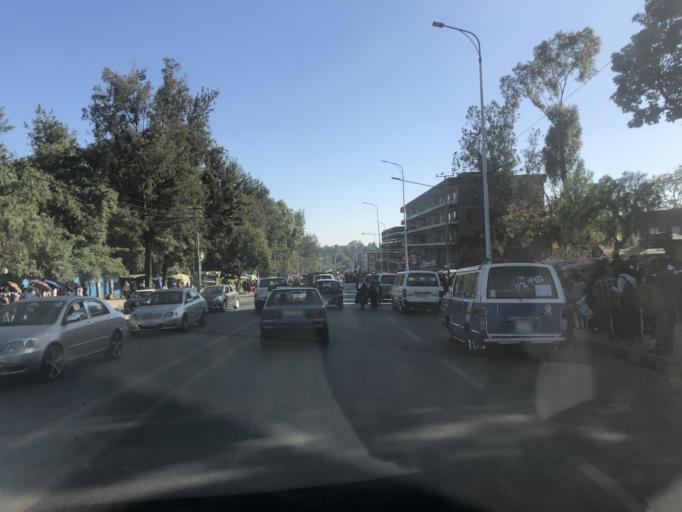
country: ET
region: Adis Abeba
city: Addis Ababa
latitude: 9.0362
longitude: 38.7629
